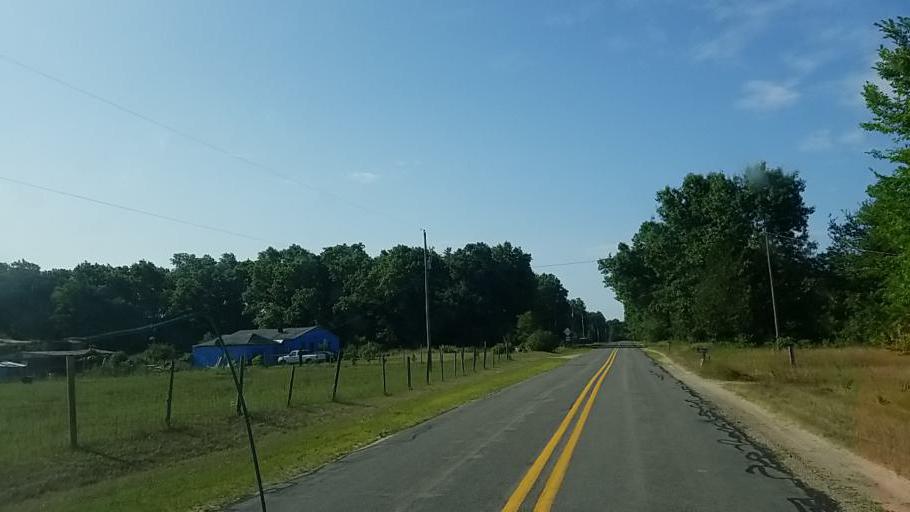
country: US
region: Michigan
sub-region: Muskegon County
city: Twin Lake
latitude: 43.4669
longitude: -86.1933
